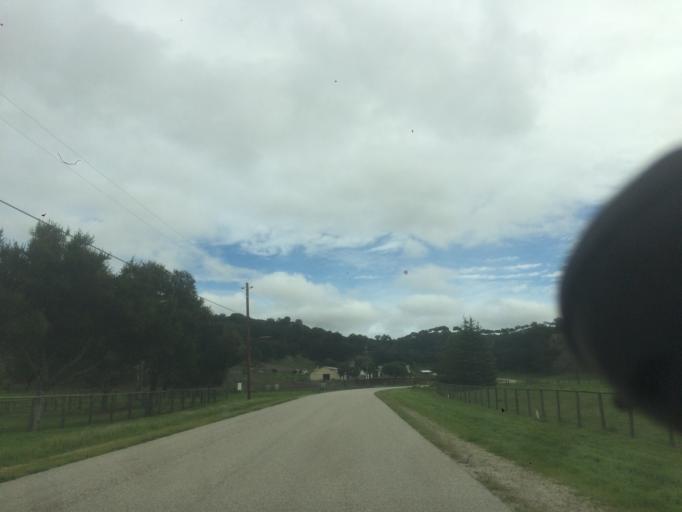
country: US
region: California
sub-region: San Luis Obispo County
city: Nipomo
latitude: 35.2073
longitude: -120.3836
